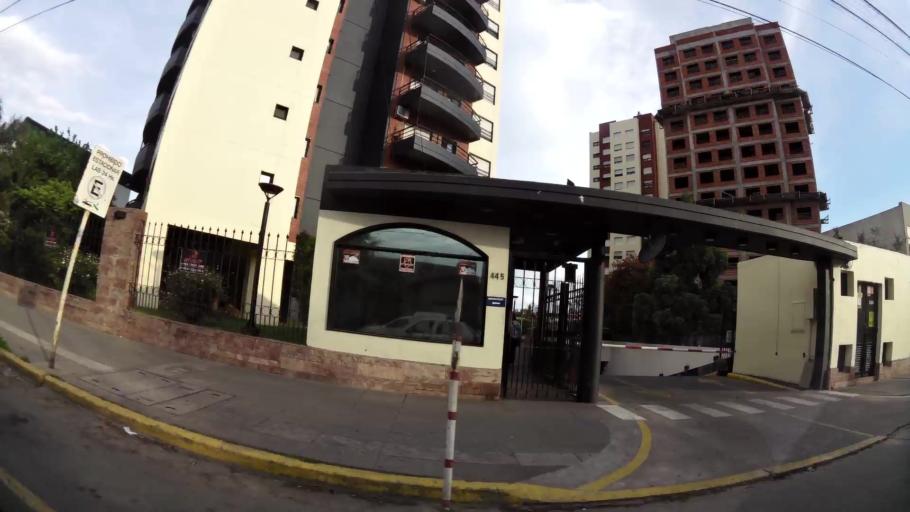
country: AR
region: Buenos Aires
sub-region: Partido de Quilmes
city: Quilmes
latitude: -34.7269
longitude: -58.2478
